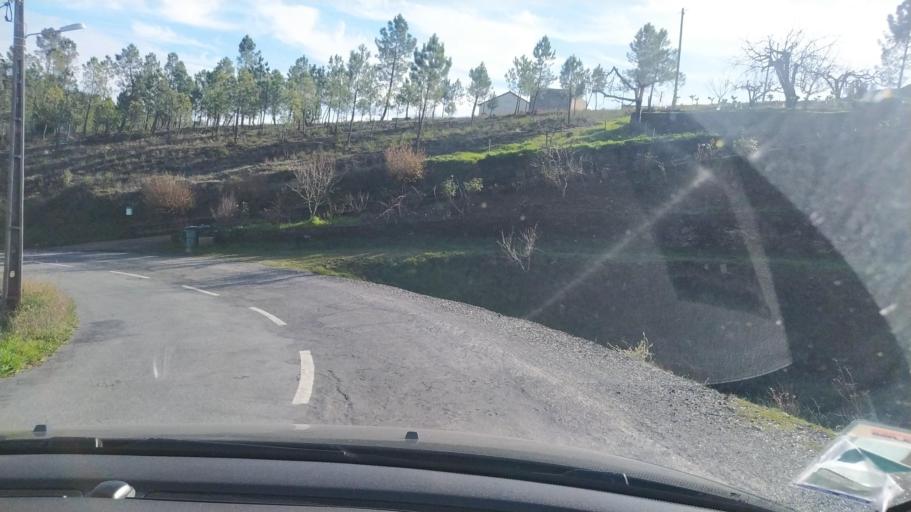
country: PT
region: Castelo Branco
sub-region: Concelho do Fundao
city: Aldeia de Joanes
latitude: 40.1824
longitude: -7.6976
